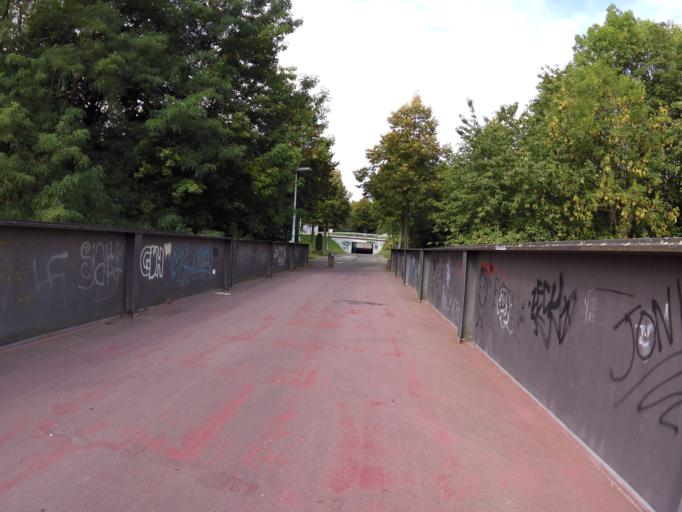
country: BE
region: Flanders
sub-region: Provincie Limburg
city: Lanaken
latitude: 50.8872
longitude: 5.6582
